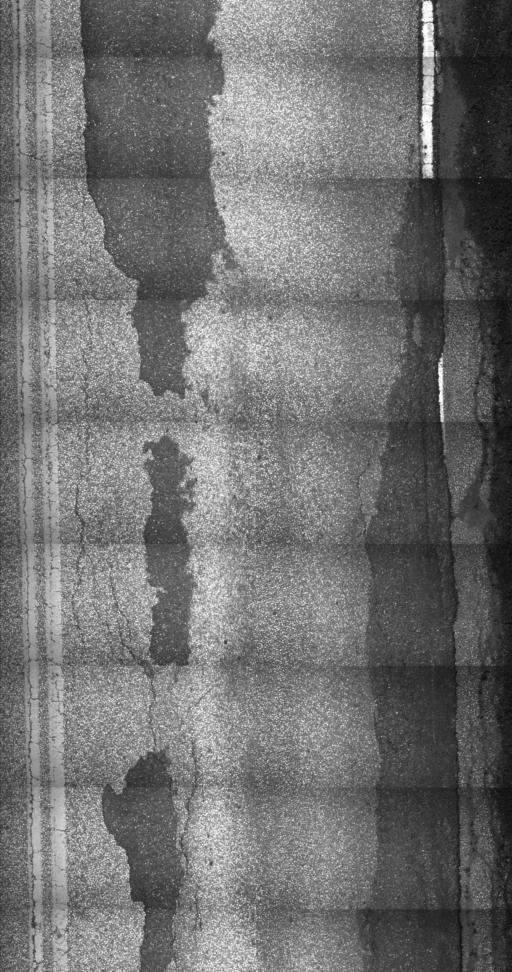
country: US
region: Vermont
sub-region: Washington County
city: Northfield
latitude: 44.0919
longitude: -72.6488
